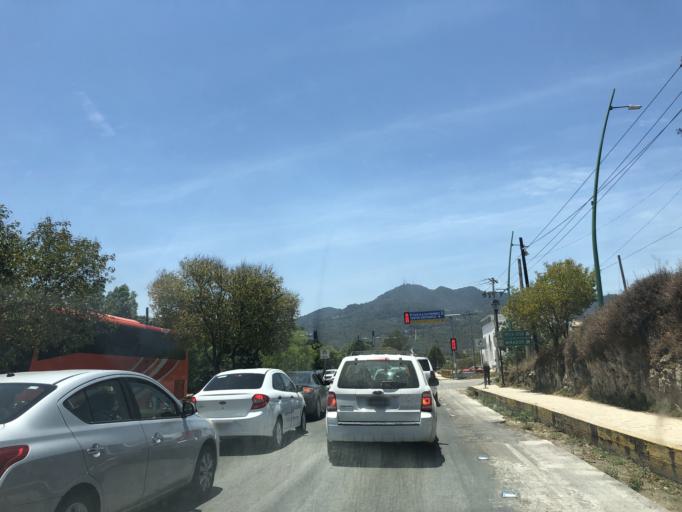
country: MX
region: Chiapas
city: San Cristobal de las Casas
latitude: 16.7319
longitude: -92.6486
